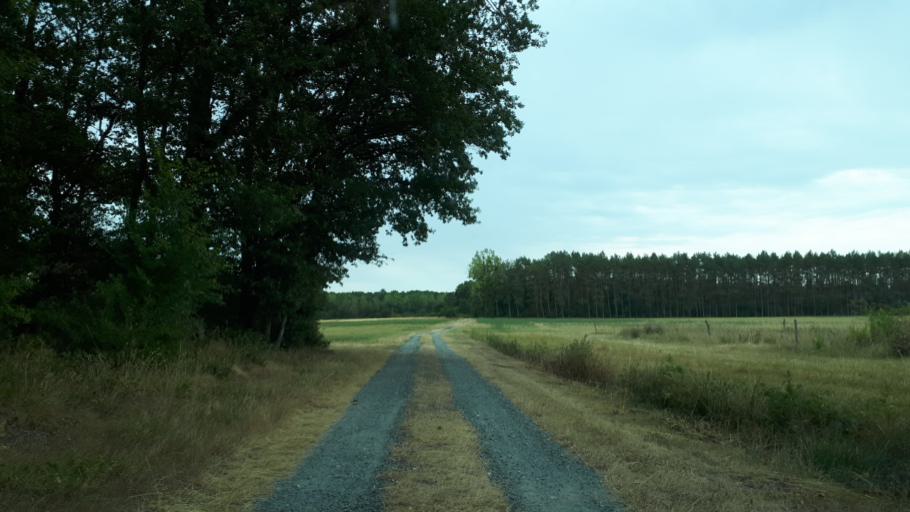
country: FR
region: Centre
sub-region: Departement du Loir-et-Cher
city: Saint-Romain-sur-Cher
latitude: 47.3529
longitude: 1.3947
